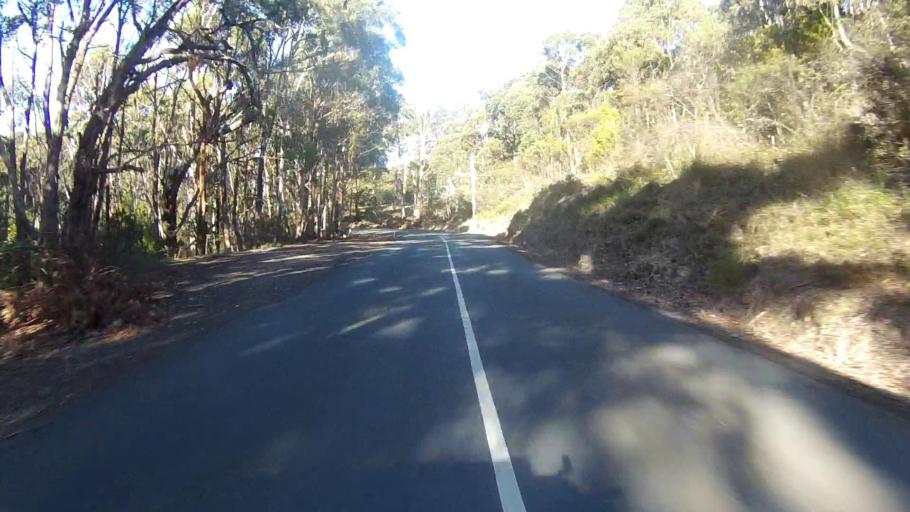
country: AU
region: Tasmania
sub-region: Clarence
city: Sandford
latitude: -43.0307
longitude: 147.9276
